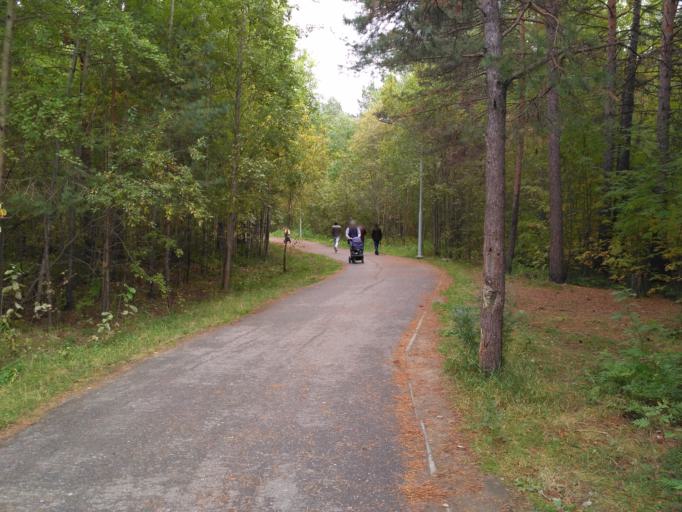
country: RU
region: Khanty-Mansiyskiy Avtonomnyy Okrug
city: Surgut
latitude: 61.2452
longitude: 73.4335
